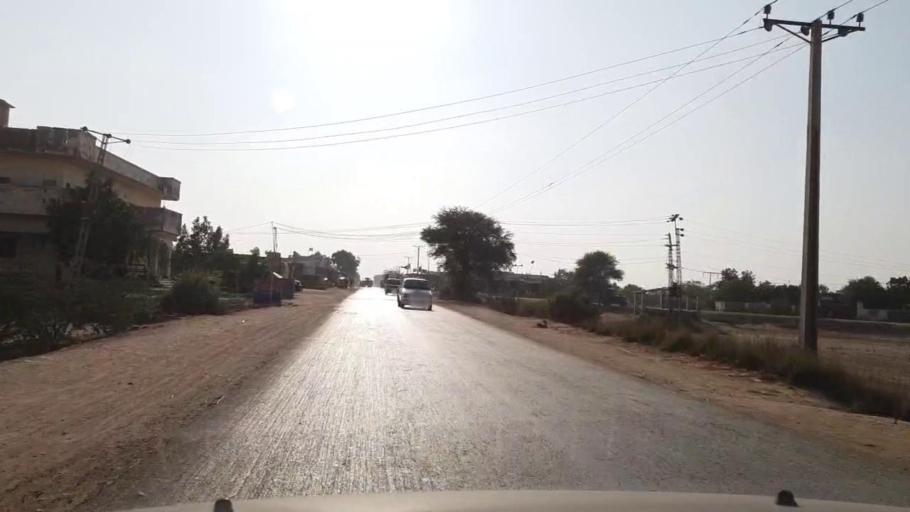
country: PK
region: Sindh
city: Bulri
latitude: 25.0090
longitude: 68.4001
